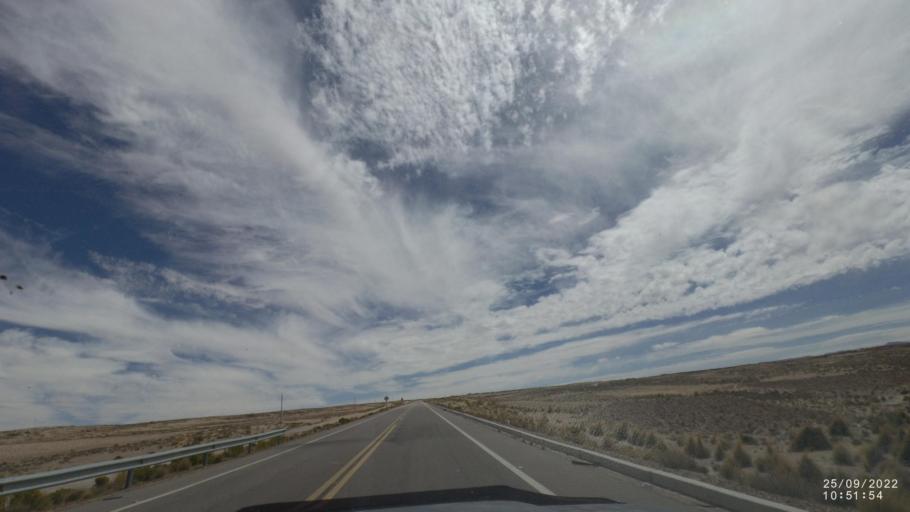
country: BO
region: Oruro
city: Challapata
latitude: -19.5563
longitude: -66.8527
